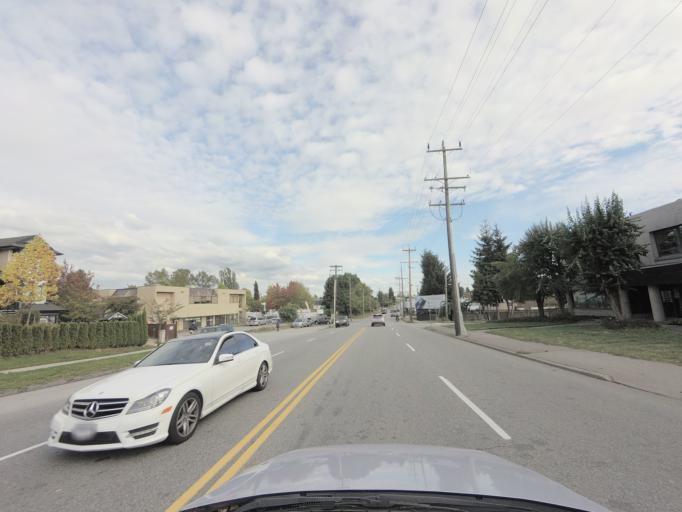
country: CA
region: British Columbia
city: New Westminster
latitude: 49.2152
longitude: -122.9405
